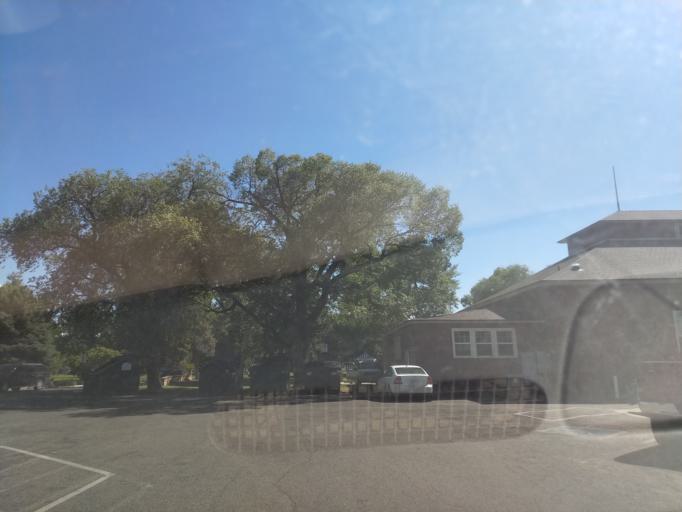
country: US
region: Colorado
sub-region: Mesa County
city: Grand Junction
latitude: 39.0756
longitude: -108.5511
